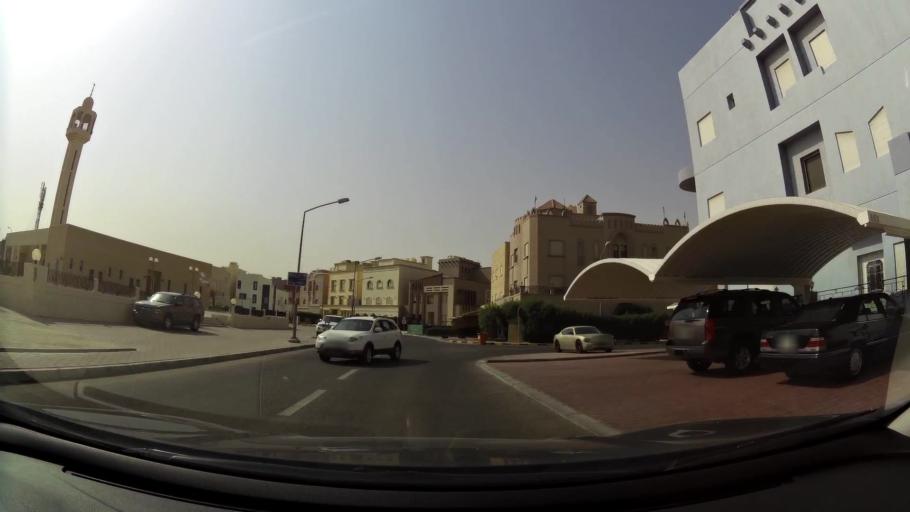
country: KW
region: Muhafazat al Jahra'
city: Al Jahra'
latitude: 29.3345
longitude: 47.7608
